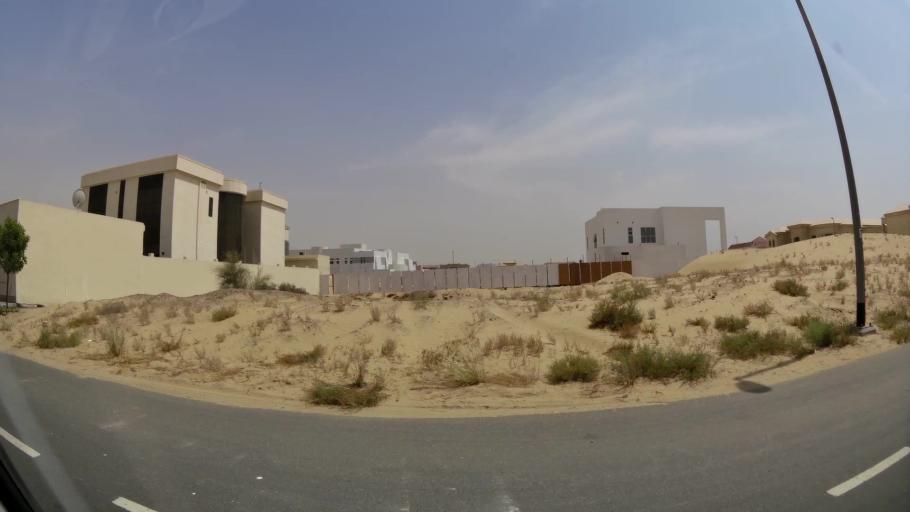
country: AE
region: Ash Shariqah
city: Sharjah
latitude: 25.2528
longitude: 55.4928
